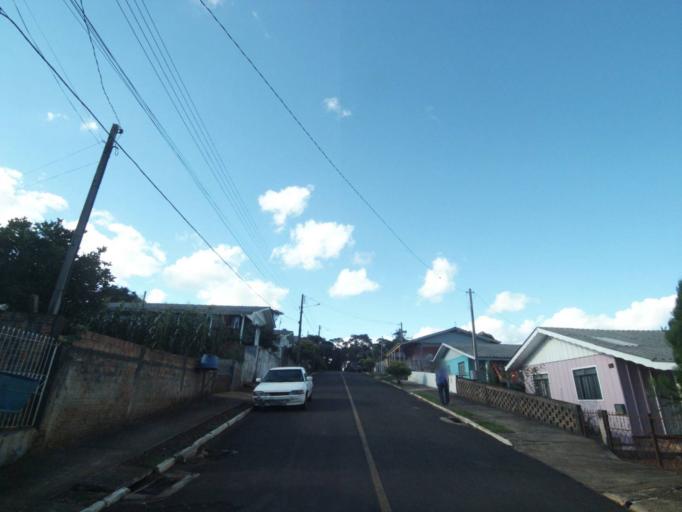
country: BR
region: Parana
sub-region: Uniao Da Vitoria
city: Uniao da Vitoria
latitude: -26.1604
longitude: -51.5360
